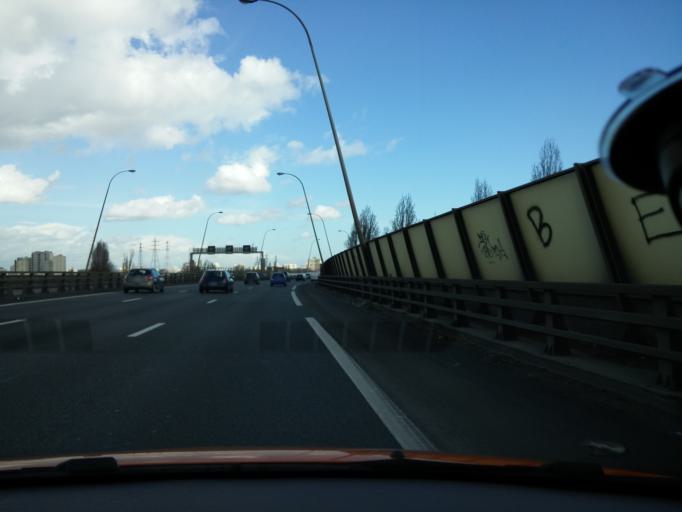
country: FR
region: Ile-de-France
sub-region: Departement du Val-de-Marne
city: Choisy-le-Roi
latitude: 48.7758
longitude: 2.4139
